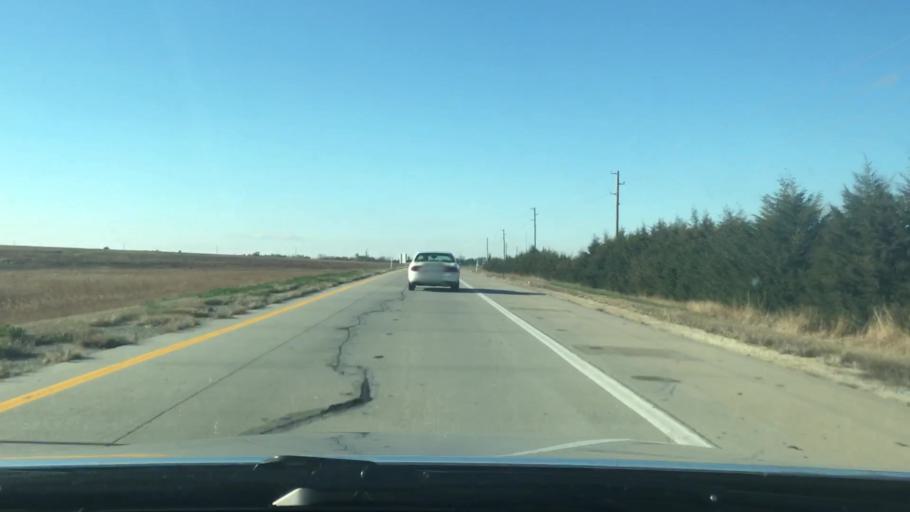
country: US
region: Kansas
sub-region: Reno County
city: South Hutchinson
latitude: 38.0151
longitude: -97.9649
